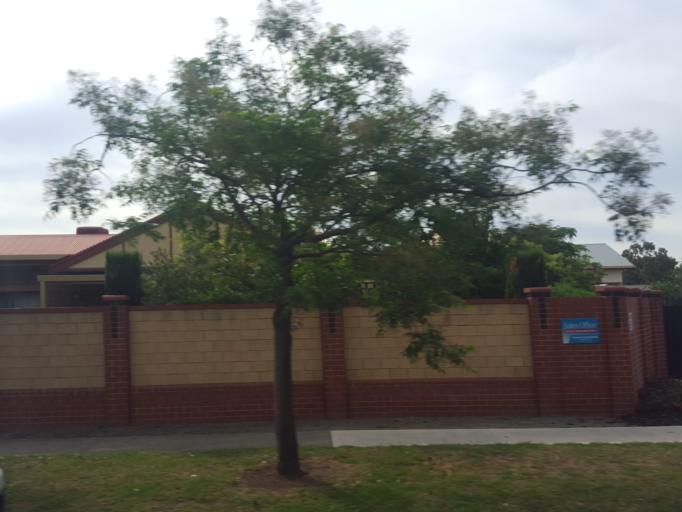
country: AU
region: South Australia
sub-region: Charles Sturt
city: Woodville
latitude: -34.8778
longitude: 138.5541
